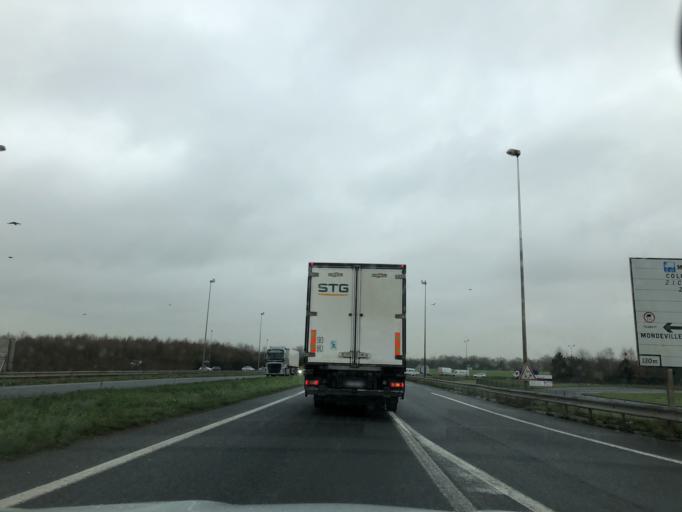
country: FR
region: Lower Normandy
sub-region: Departement du Calvados
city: Giberville
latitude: 49.1719
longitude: -0.2985
